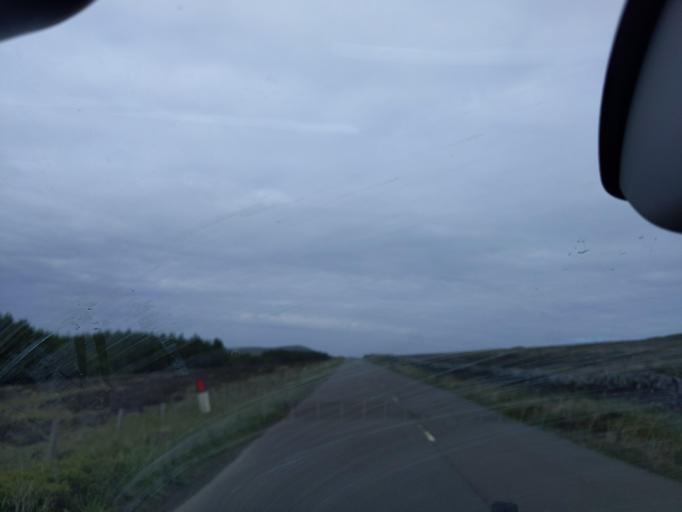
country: IM
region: Castletown
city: Castletown
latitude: 54.1501
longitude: -4.6853
